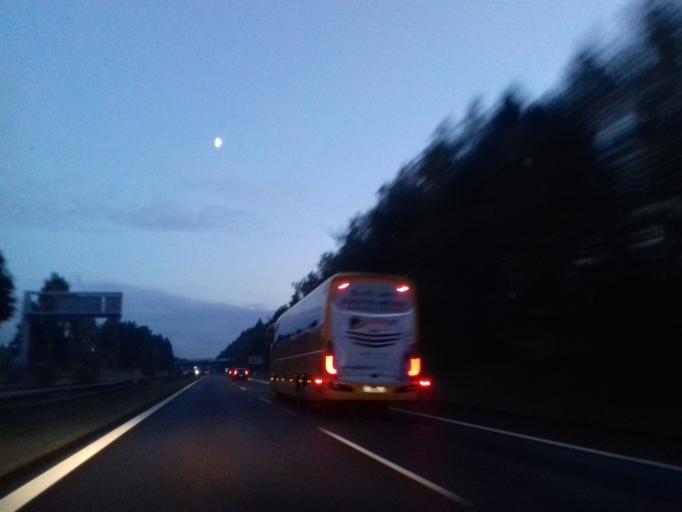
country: CZ
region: Vysocina
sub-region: Okres Pelhrimov
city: Humpolec
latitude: 49.5449
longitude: 15.3302
